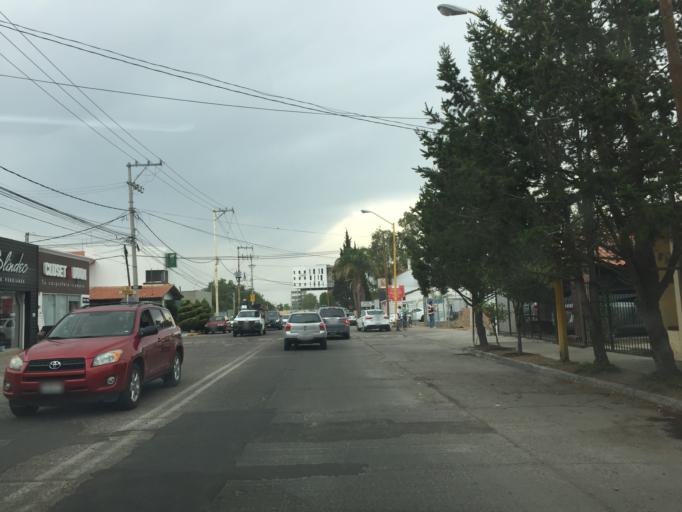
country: MX
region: Aguascalientes
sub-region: Jesus Maria
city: El Llano
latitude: 21.9291
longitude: -102.3052
